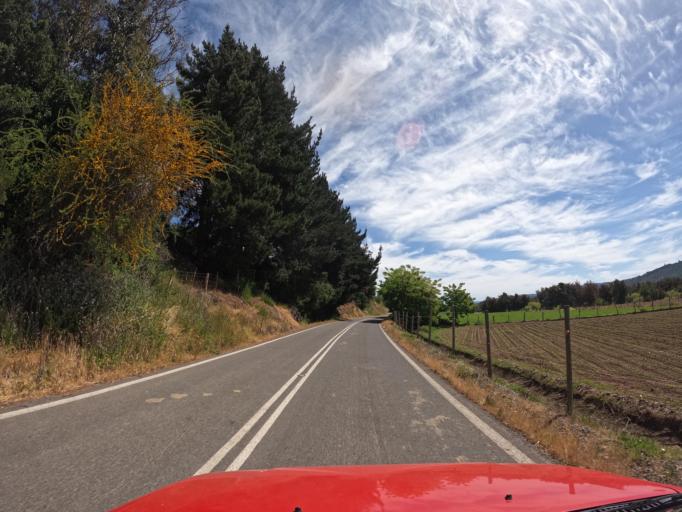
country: CL
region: Maule
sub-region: Provincia de Talca
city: Talca
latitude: -34.9905
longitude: -71.8488
